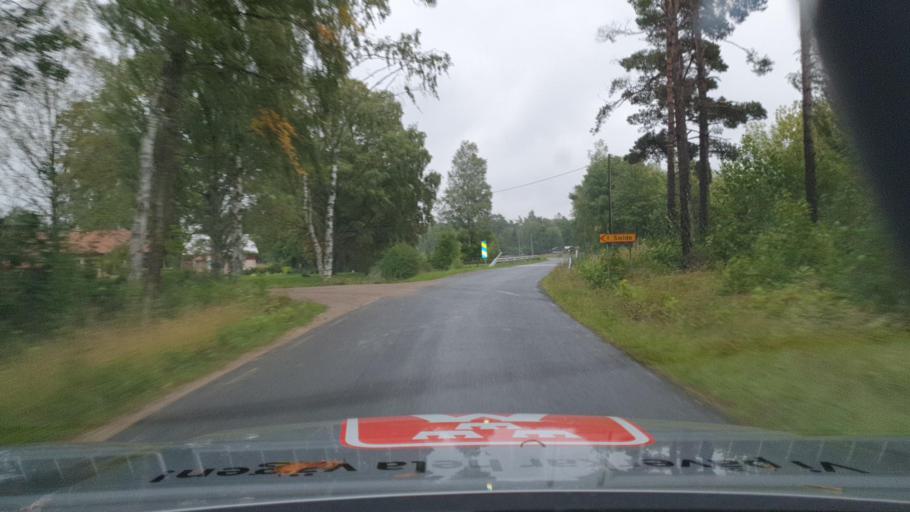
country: SE
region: Gotland
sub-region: Gotland
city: Hemse
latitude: 57.4265
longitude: 18.4090
